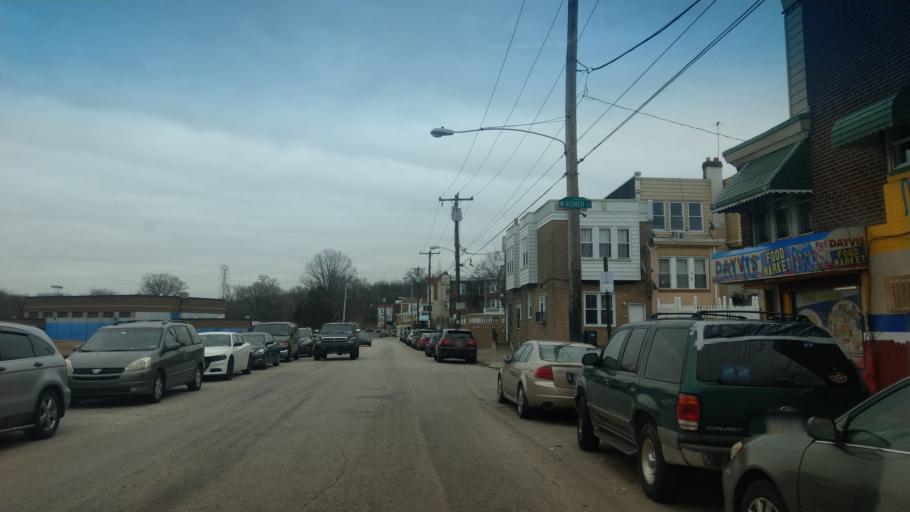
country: US
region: Pennsylvania
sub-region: Montgomery County
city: Rockledge
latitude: 40.0219
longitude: -75.1146
